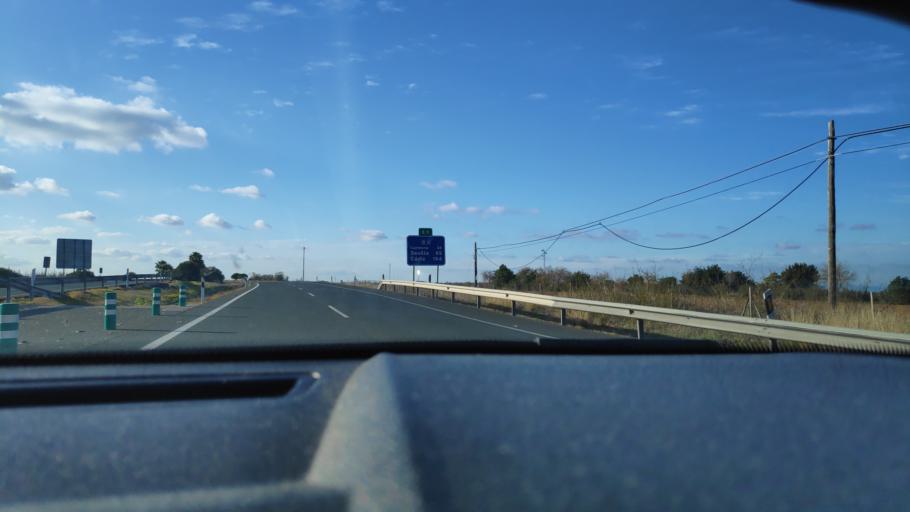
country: ES
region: Andalusia
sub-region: Provincia de Sevilla
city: La Luisiana
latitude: 37.5272
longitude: -5.2641
